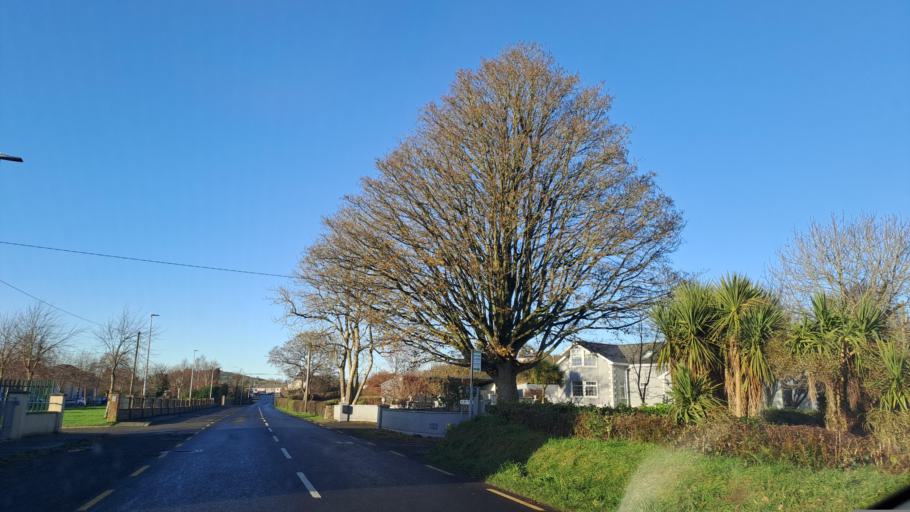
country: IE
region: Ulster
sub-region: An Cabhan
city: Mullagh
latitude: 53.8090
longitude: -6.9387
